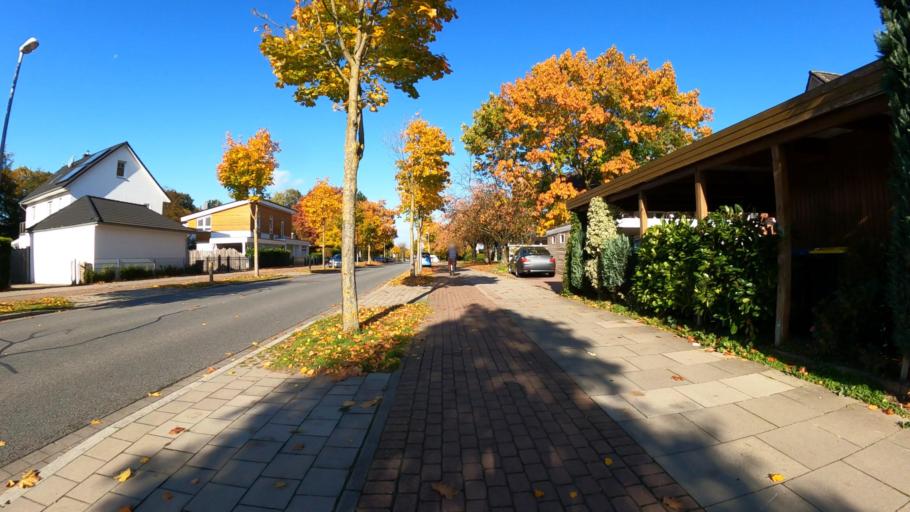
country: DE
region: Schleswig-Holstein
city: Ahrensburg
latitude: 53.6749
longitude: 10.2285
